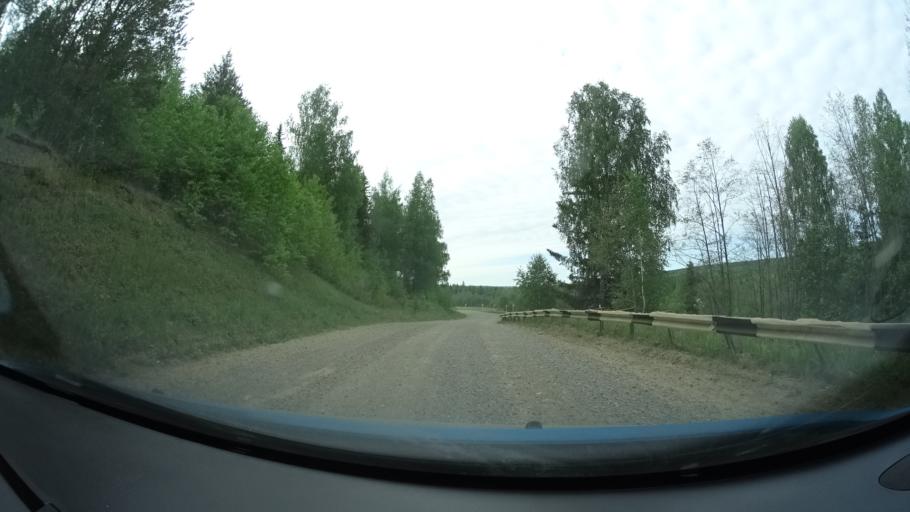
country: RU
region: Perm
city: Kuyeda
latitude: 56.6526
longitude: 55.6946
